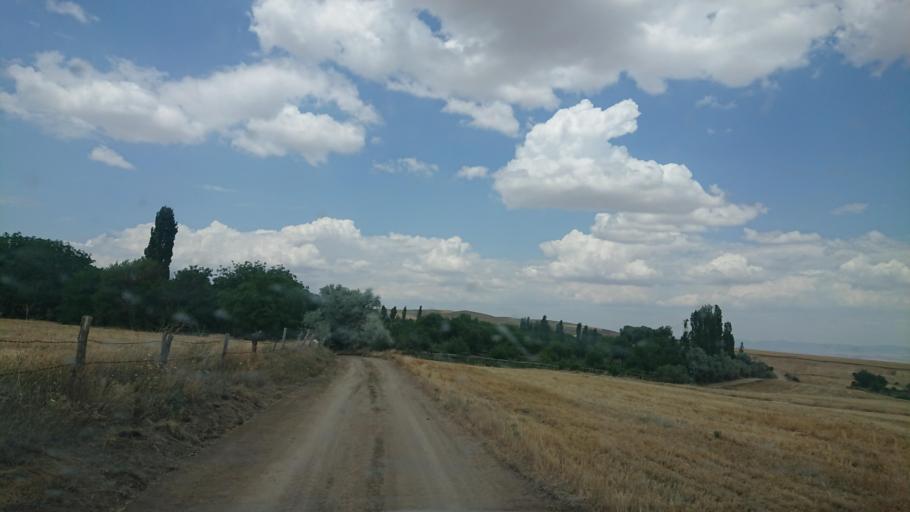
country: TR
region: Aksaray
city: Agacoren
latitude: 38.8906
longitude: 33.8825
